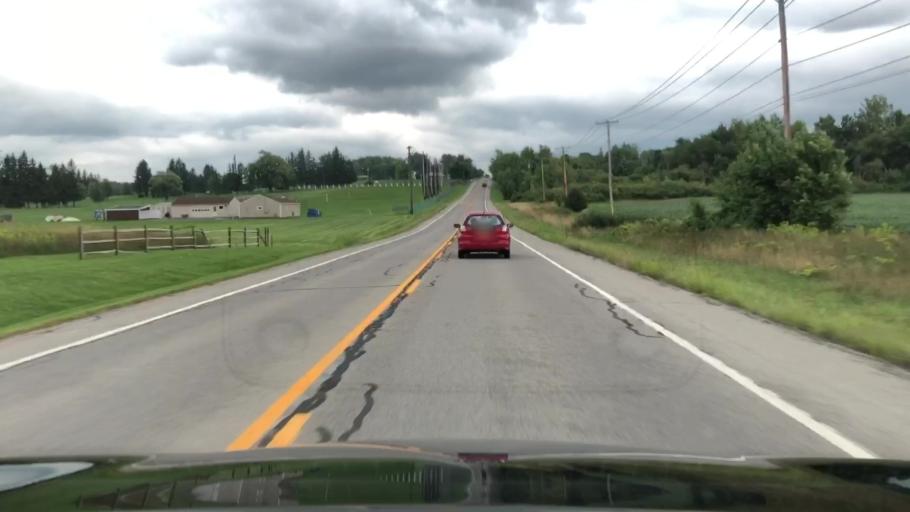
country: US
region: New York
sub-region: Erie County
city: Orchard Park
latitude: 42.7765
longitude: -78.6969
